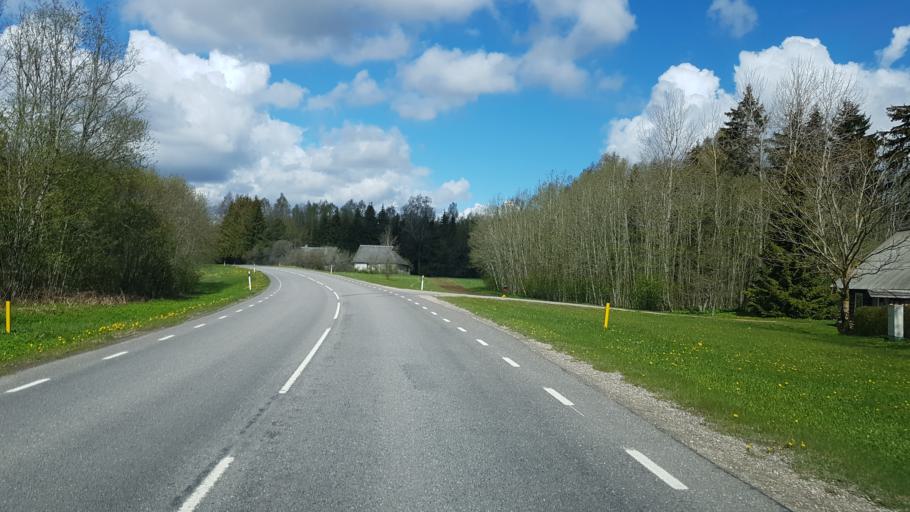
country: EE
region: Raplamaa
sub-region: Kehtna vald
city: Kehtna
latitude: 59.0517
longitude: 25.0216
